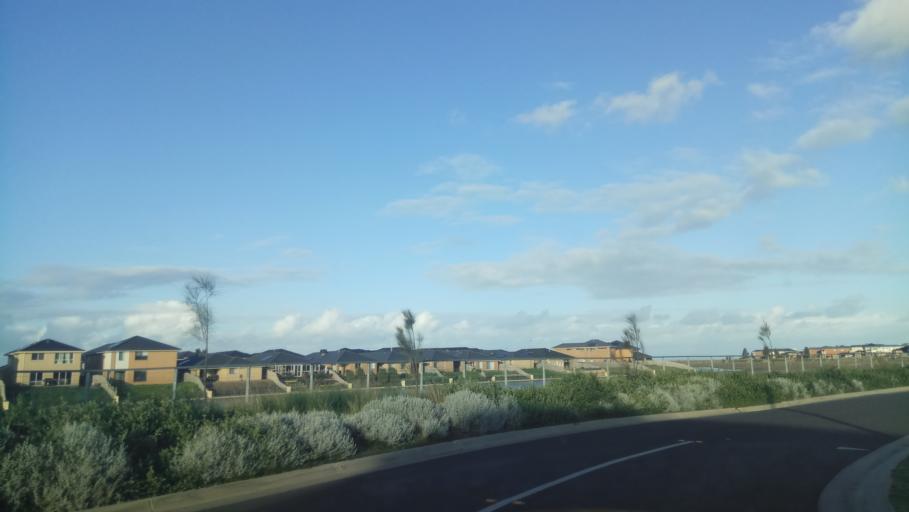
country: AU
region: Victoria
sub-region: Wyndham
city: Point Cook
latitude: -37.9045
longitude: 144.7718
